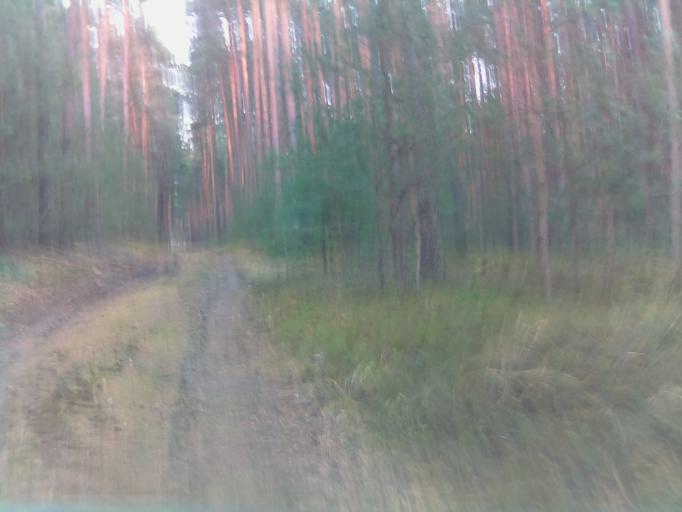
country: DE
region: Brandenburg
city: Tauer
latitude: 51.9665
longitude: 14.4537
